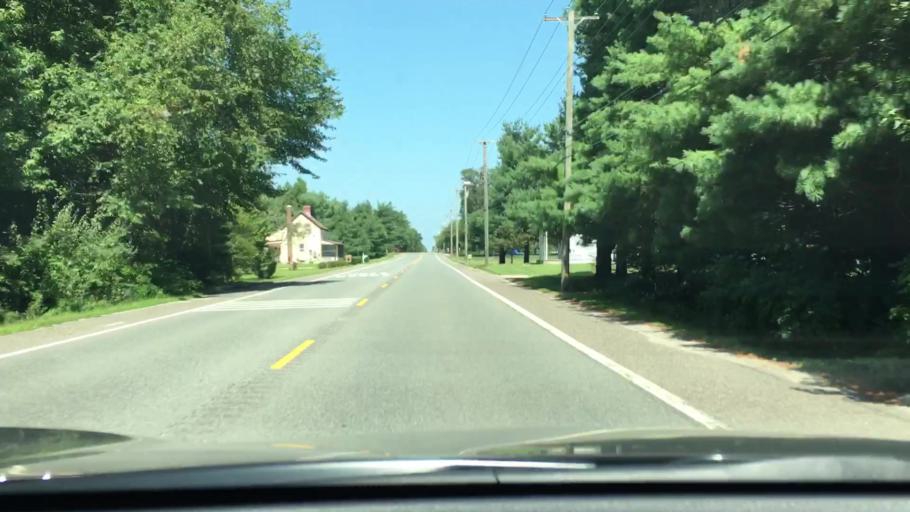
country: US
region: New Jersey
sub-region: Cumberland County
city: Laurel Lake
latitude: 39.2912
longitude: -74.9962
